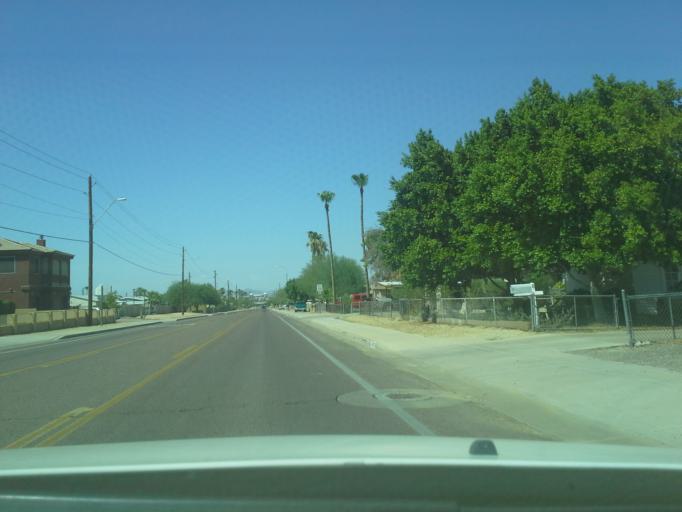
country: US
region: Arizona
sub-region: Maricopa County
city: Phoenix
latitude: 33.3673
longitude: -112.0659
